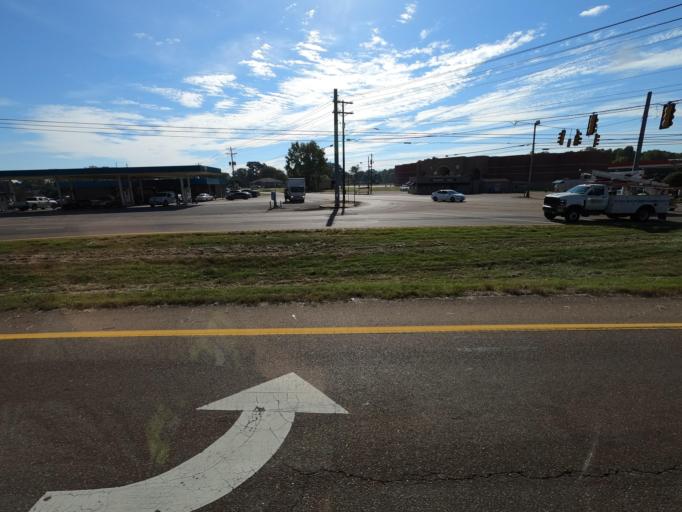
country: US
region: Tennessee
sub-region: Tipton County
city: Atoka
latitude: 35.4447
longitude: -89.7885
